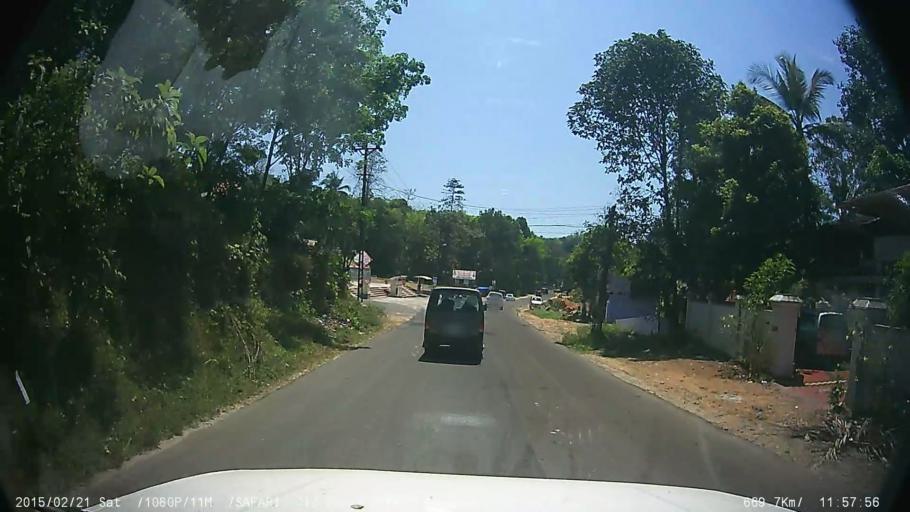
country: IN
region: Kerala
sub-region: Kottayam
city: Lalam
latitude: 9.7361
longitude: 76.6917
